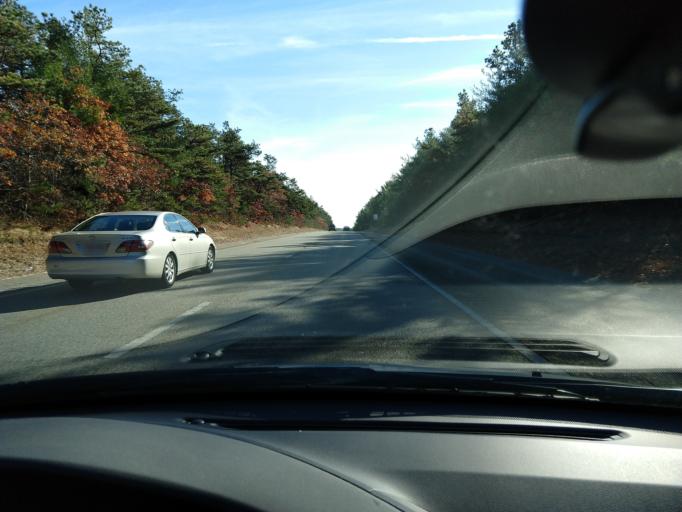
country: US
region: Massachusetts
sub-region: Plymouth County
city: White Island Shores
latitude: 41.8437
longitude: -70.5726
